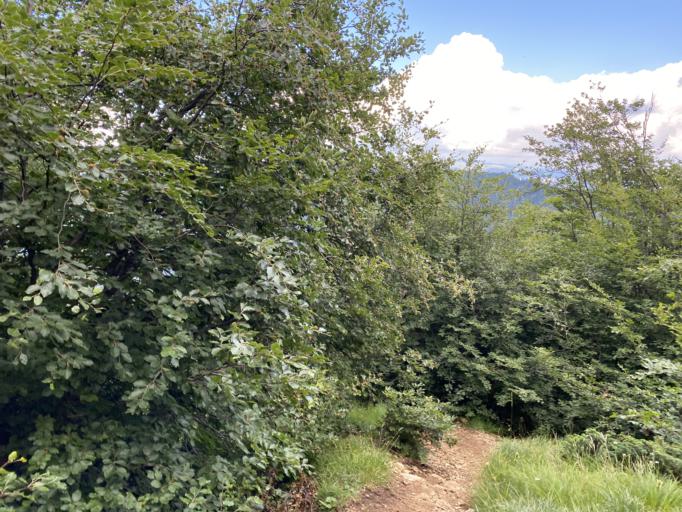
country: IT
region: Veneto
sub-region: Provincia di Verona
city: Ferrara di Monte Baldo
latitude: 45.7140
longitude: 10.8536
